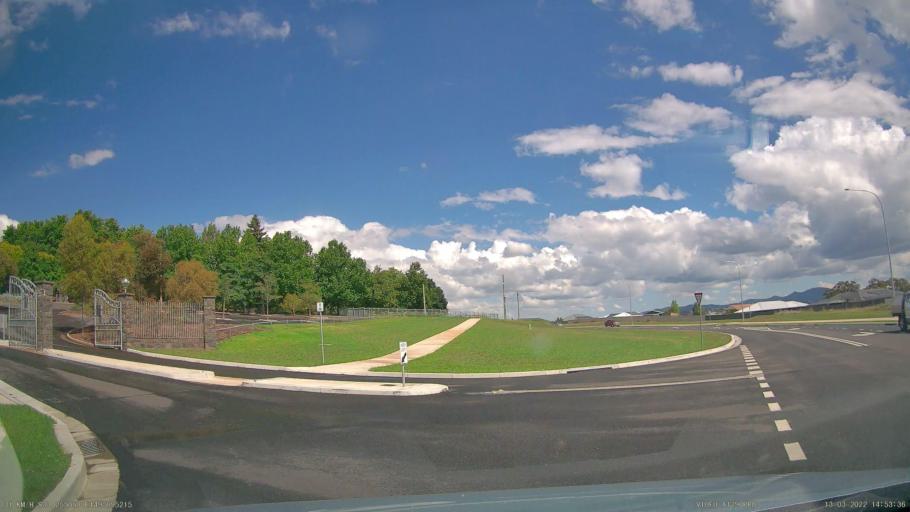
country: AU
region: New South Wales
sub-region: Orange Municipality
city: Orange
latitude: -33.2551
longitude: 149.0953
